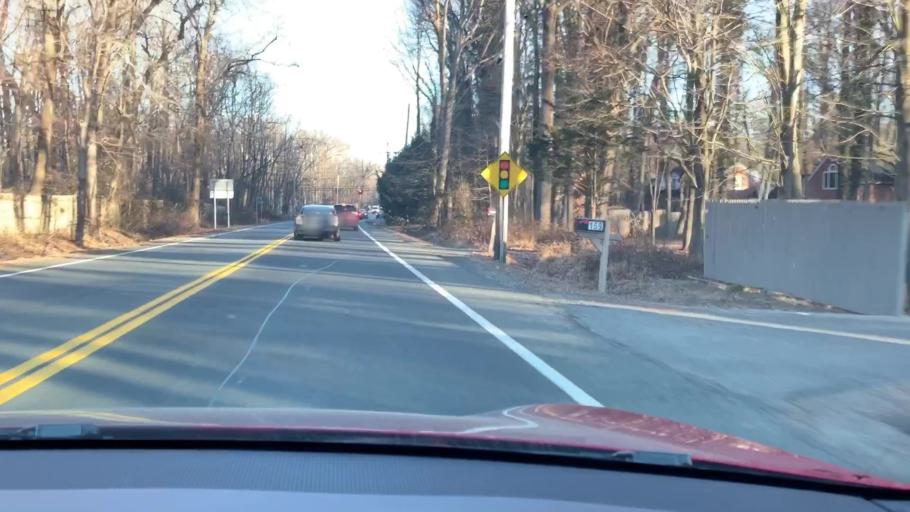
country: US
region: New York
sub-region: Rockland County
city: Sparkill
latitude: 41.0098
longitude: -73.9134
